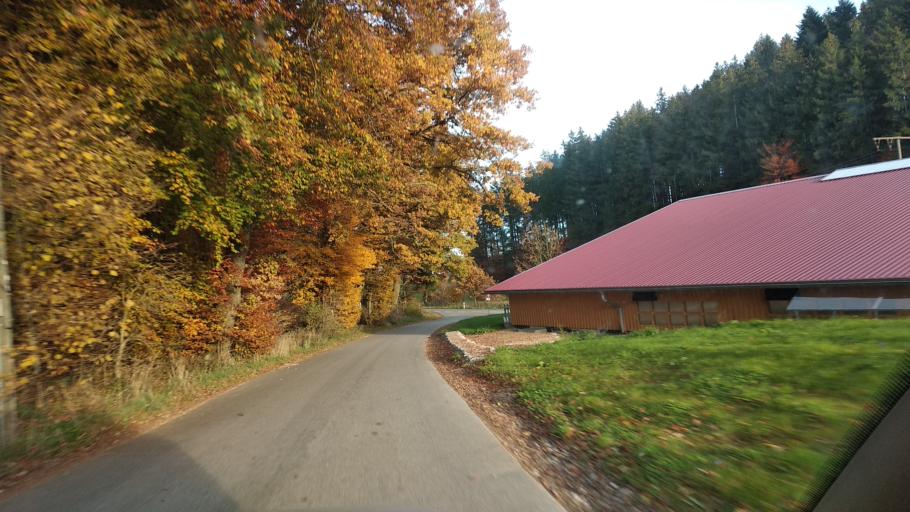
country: DE
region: Bavaria
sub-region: Upper Bavaria
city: Bruck
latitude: 48.0366
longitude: 11.9010
